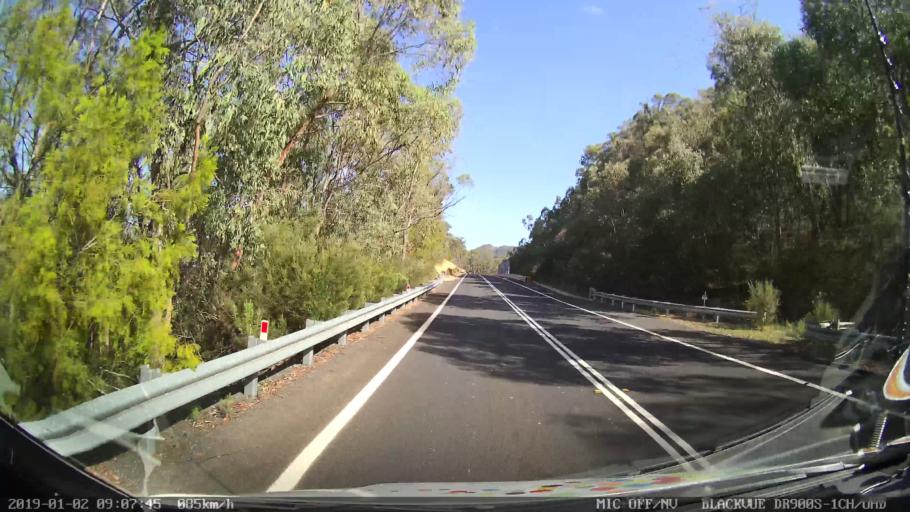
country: AU
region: New South Wales
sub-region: Tumut Shire
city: Tumut
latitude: -35.5375
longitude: 148.2965
